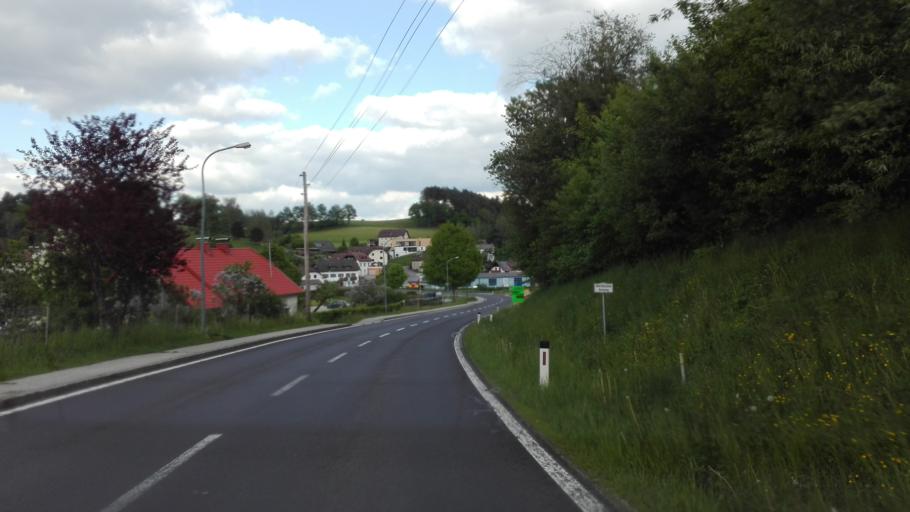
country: AT
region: Upper Austria
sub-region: Politischer Bezirk Perg
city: Bad Kreuzen
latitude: 48.3936
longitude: 14.7268
